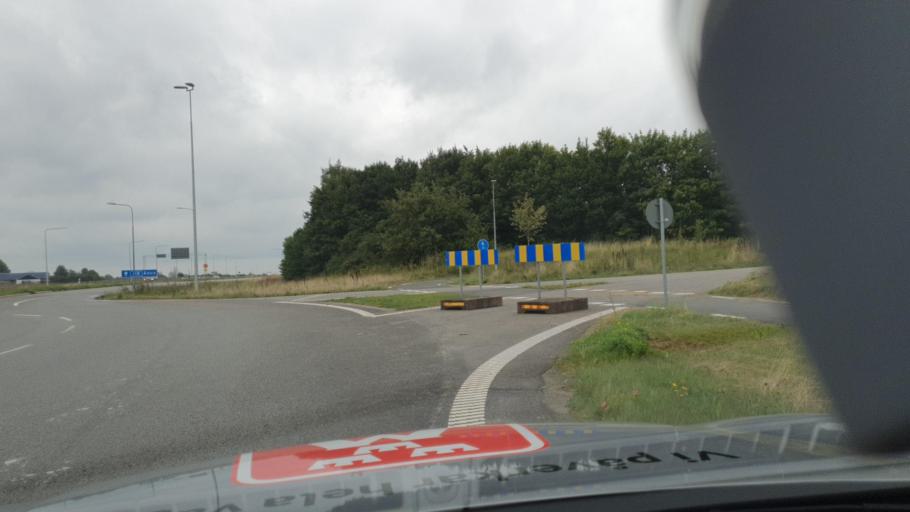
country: SE
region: Skane
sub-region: Kristianstads Kommun
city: Kristianstad
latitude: 56.0244
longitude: 14.2115
